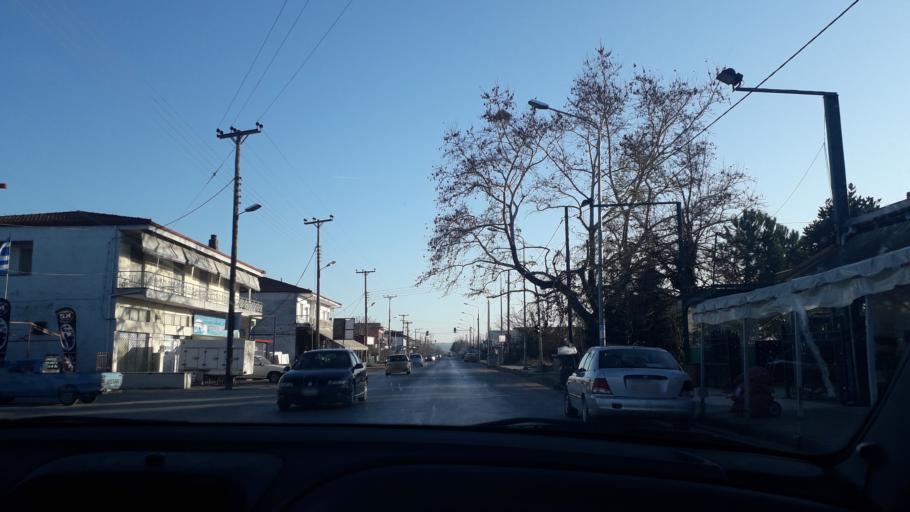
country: GR
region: Central Macedonia
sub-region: Nomos Imathias
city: Alexandreia
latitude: 40.6208
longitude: 22.4473
